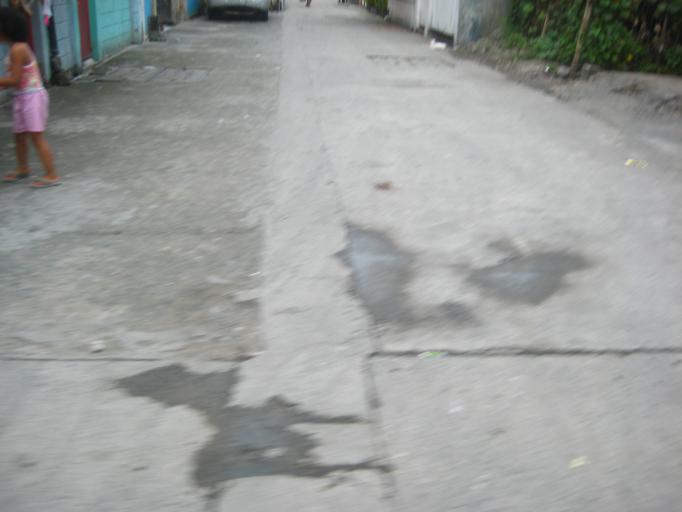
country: PH
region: Calabarzon
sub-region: Province of Rizal
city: Pateros
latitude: 14.5443
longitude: 121.0705
